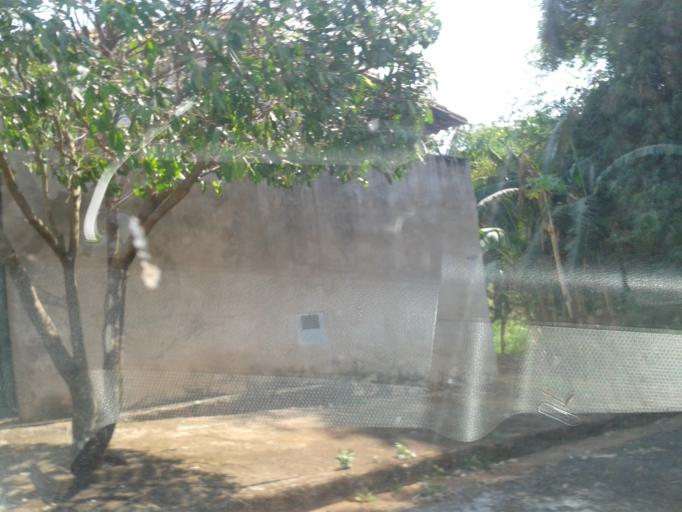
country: BR
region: Minas Gerais
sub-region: Ituiutaba
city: Ituiutaba
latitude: -18.9674
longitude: -49.4845
